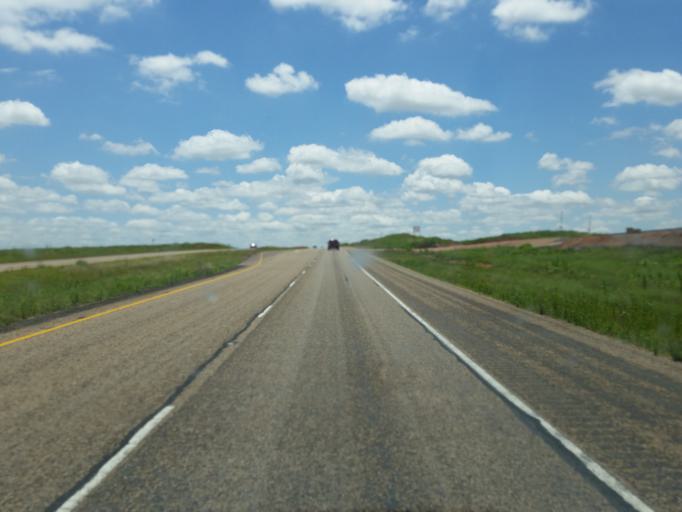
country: US
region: Texas
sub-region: Garza County
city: Post
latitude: 33.1112
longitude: -101.2712
